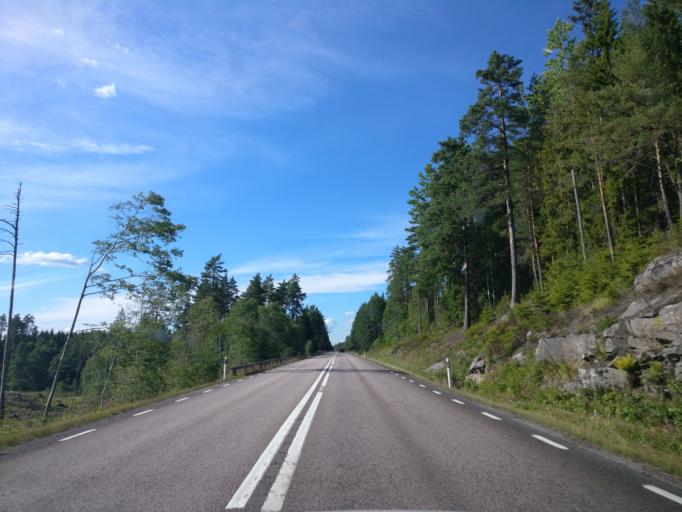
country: SE
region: Vaermland
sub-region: Karlstads Kommun
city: Edsvalla
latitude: 59.5853
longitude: 13.0139
